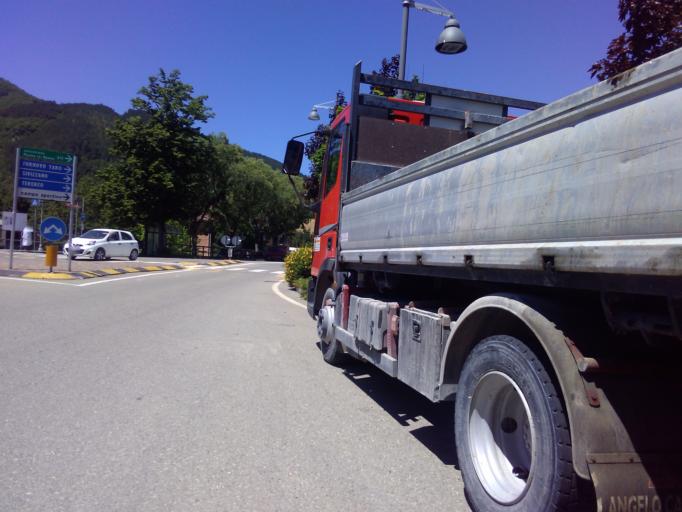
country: IT
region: Emilia-Romagna
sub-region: Provincia di Parma
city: Calestano
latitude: 44.6011
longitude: 10.1215
